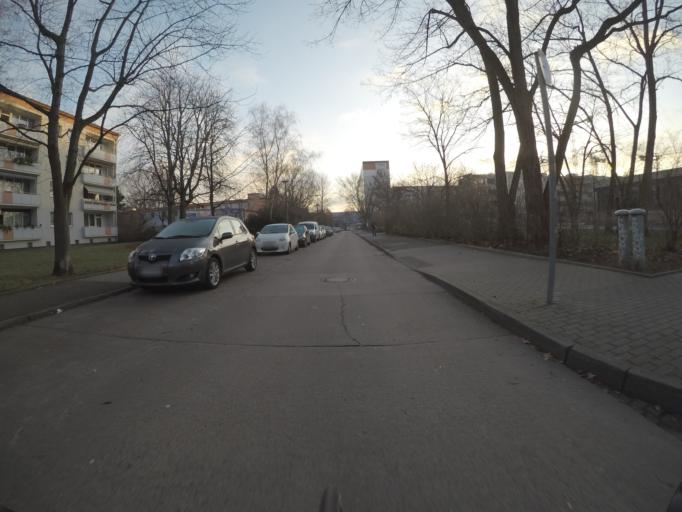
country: DE
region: Berlin
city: Friedrichsfelde
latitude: 52.4956
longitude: 13.5055
